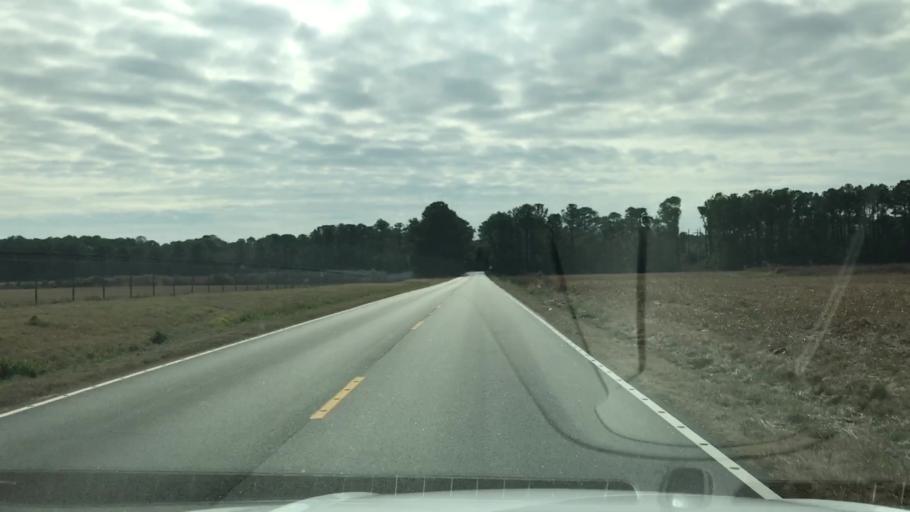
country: US
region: South Carolina
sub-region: Charleston County
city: Folly Beach
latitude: 32.7051
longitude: -80.0162
